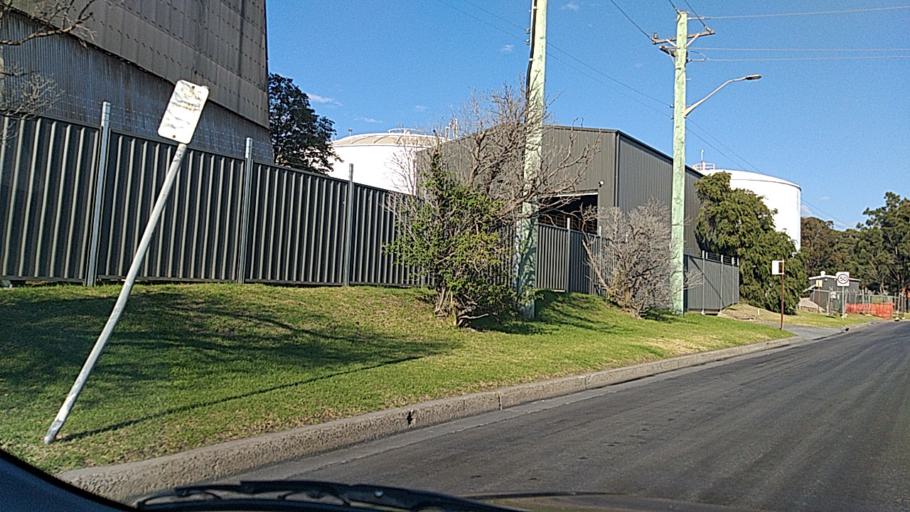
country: AU
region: New South Wales
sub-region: Wollongong
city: Port Kembla
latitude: -34.4758
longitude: 150.9114
